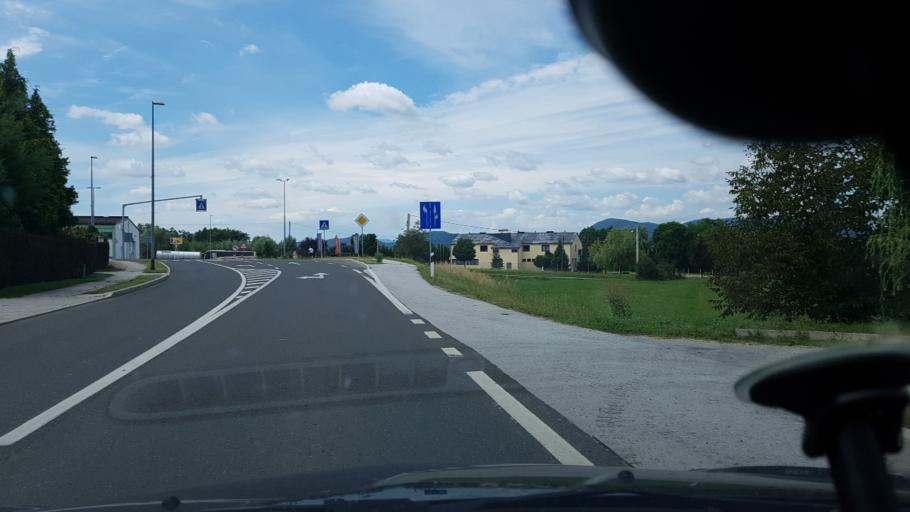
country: HR
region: Varazdinska
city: Ivanec
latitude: 46.2262
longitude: 16.1112
